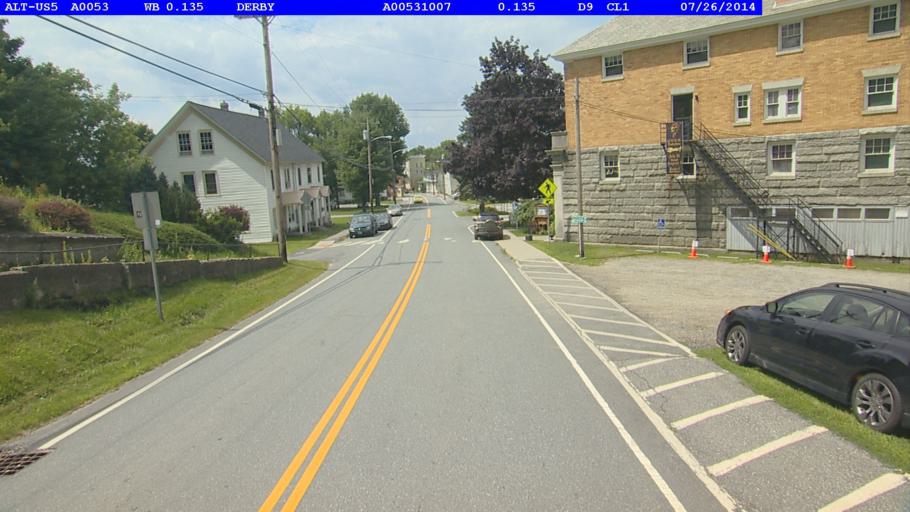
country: US
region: Vermont
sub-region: Orleans County
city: Newport
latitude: 45.0056
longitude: -72.0972
